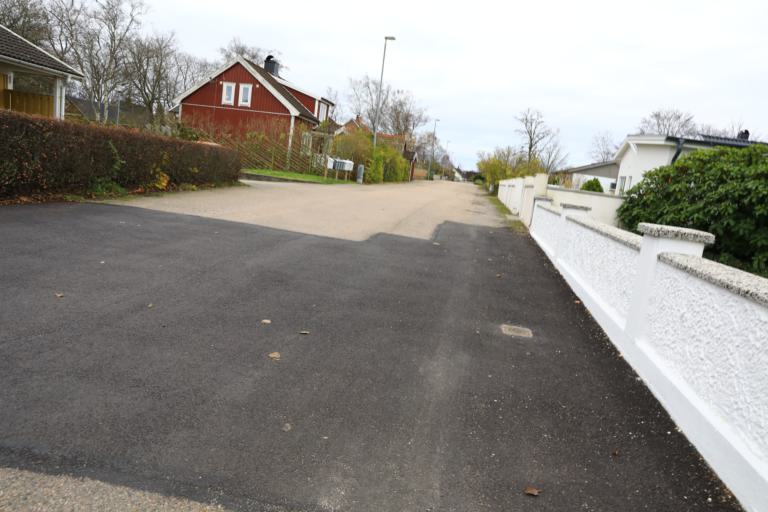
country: SE
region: Halland
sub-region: Varbergs Kommun
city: Tvaaker
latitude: 57.0416
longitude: 12.3972
